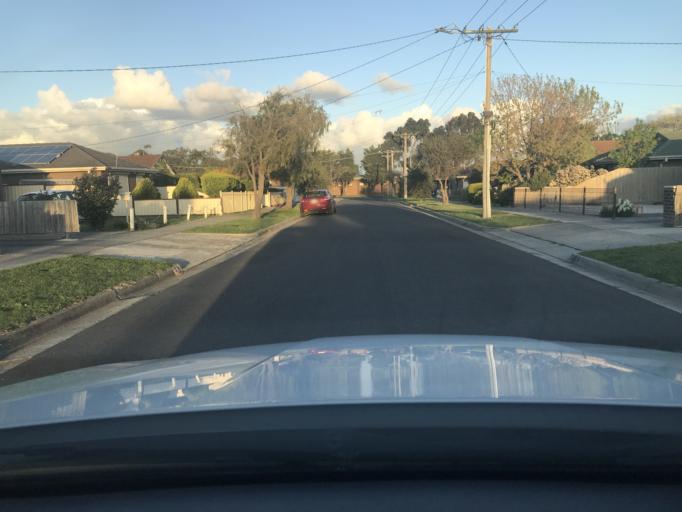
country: AU
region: Victoria
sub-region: Hume
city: Craigieburn
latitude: -37.5967
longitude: 144.9304
